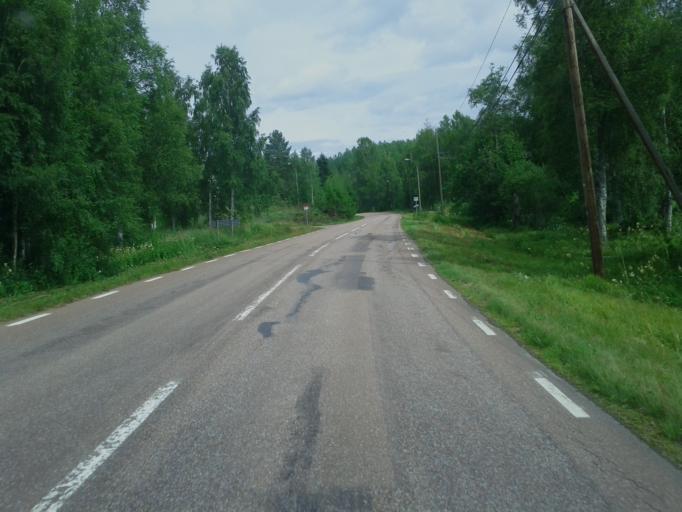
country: SE
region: Dalarna
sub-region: Smedjebackens Kommun
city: Smedjebacken
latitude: 60.3129
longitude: 15.3738
